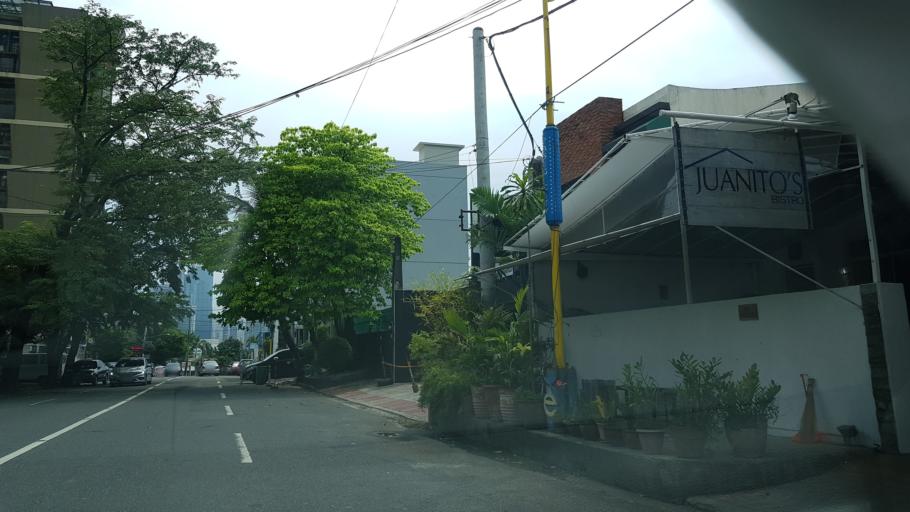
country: PH
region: Metro Manila
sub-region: Pasig
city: Pasig City
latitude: 14.5692
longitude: 121.0601
